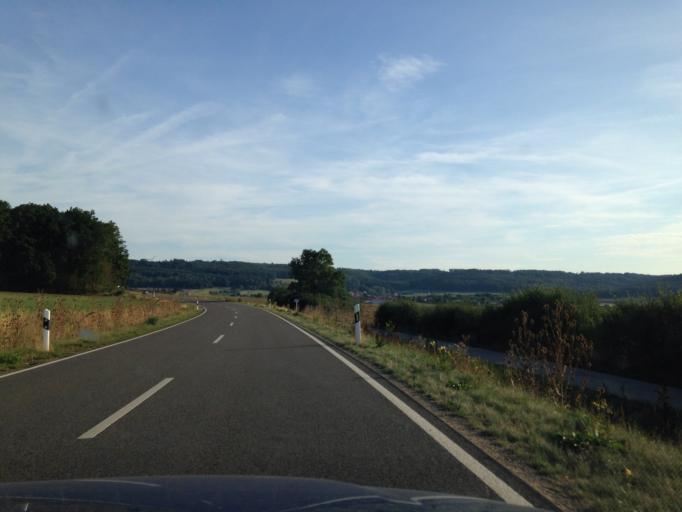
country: DE
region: Bavaria
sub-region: Regierungsbezirk Mittelfranken
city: Thalmassing
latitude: 49.1027
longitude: 11.2170
